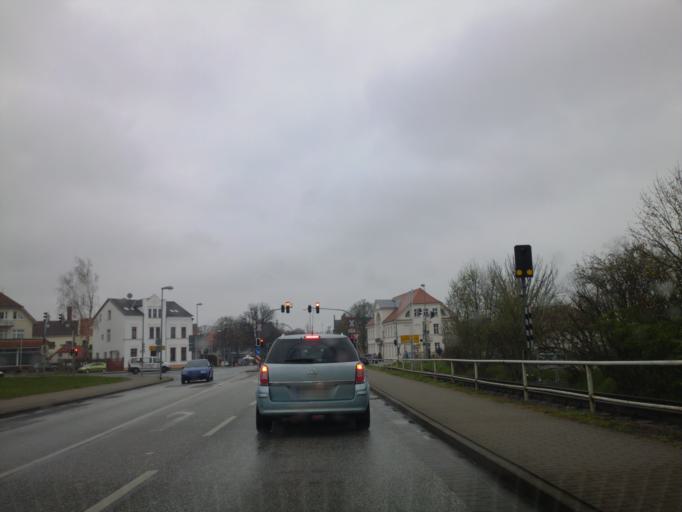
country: DE
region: Mecklenburg-Vorpommern
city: Bad Doberan
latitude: 54.1024
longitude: 11.9022
